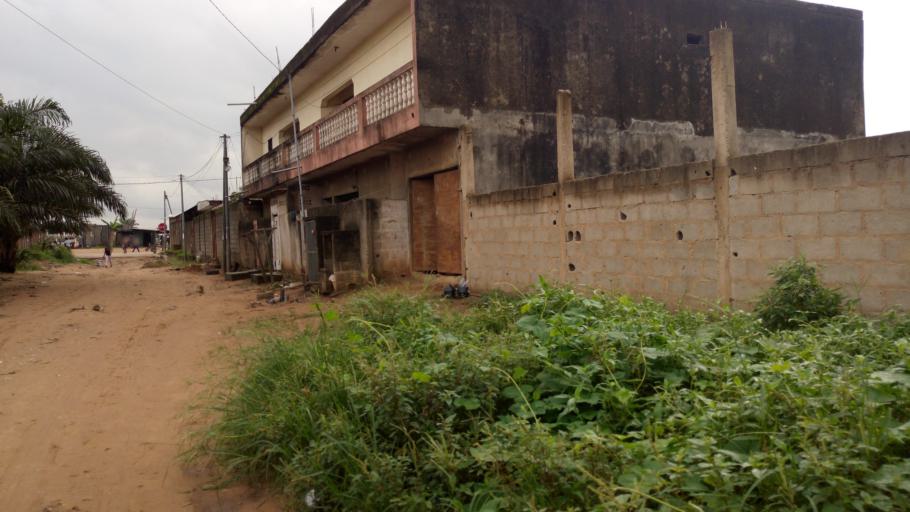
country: CI
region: Lagunes
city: Abobo
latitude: 5.4111
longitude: -3.9969
